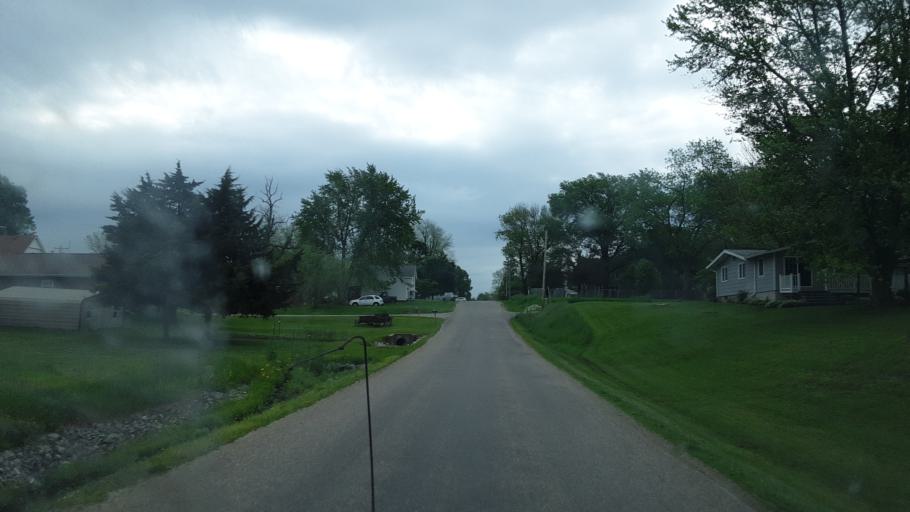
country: US
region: Illinois
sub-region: Fulton County
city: Astoria
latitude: 40.3642
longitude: -90.4278
